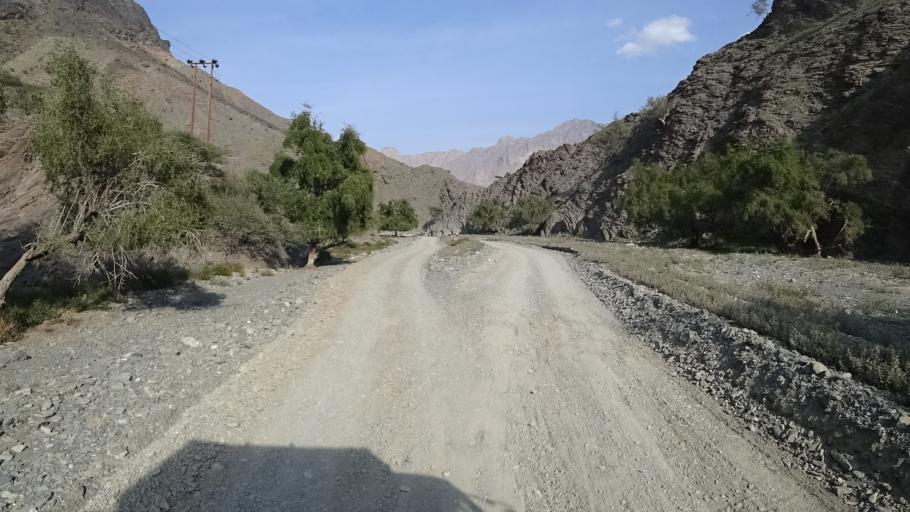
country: OM
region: Al Batinah
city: Bayt al `Awabi
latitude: 23.2552
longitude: 57.4098
